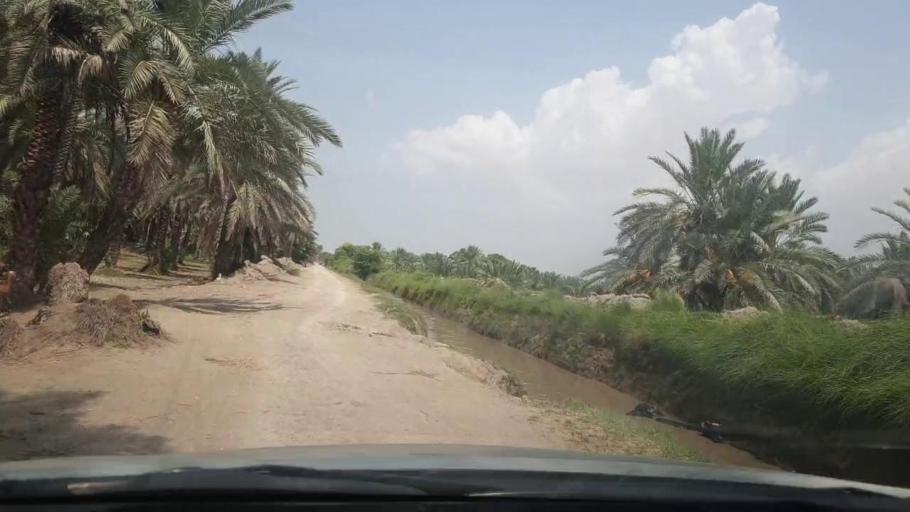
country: PK
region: Sindh
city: Khairpur
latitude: 27.5487
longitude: 68.8476
